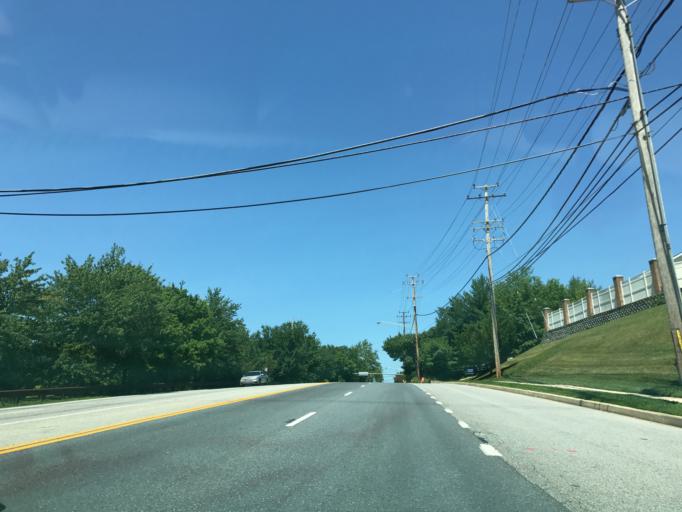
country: US
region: Maryland
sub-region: Baltimore County
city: Garrison
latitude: 39.3912
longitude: -76.7416
